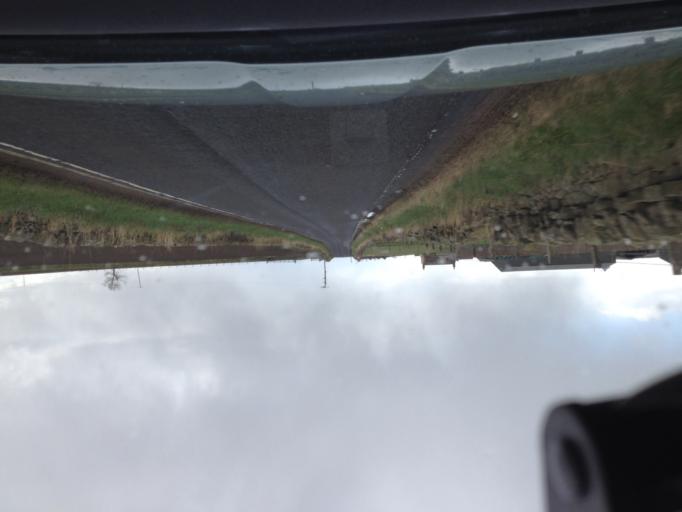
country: GB
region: Scotland
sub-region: West Lothian
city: Livingston
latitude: 55.9404
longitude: -3.5505
